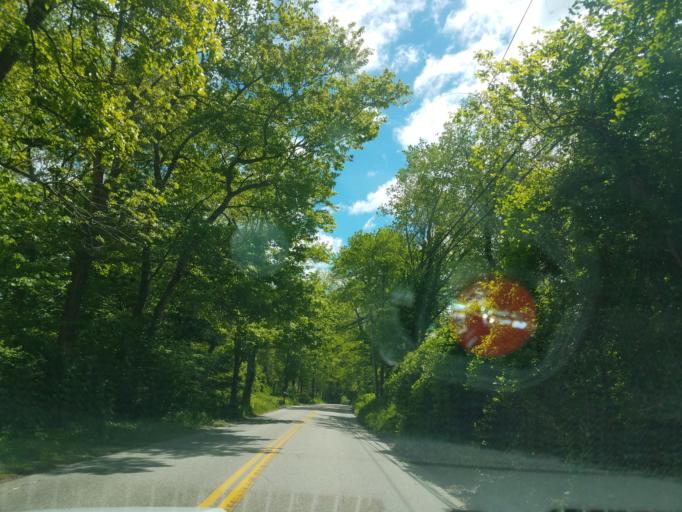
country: US
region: Connecticut
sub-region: New London County
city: Colchester
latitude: 41.4998
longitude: -72.2908
